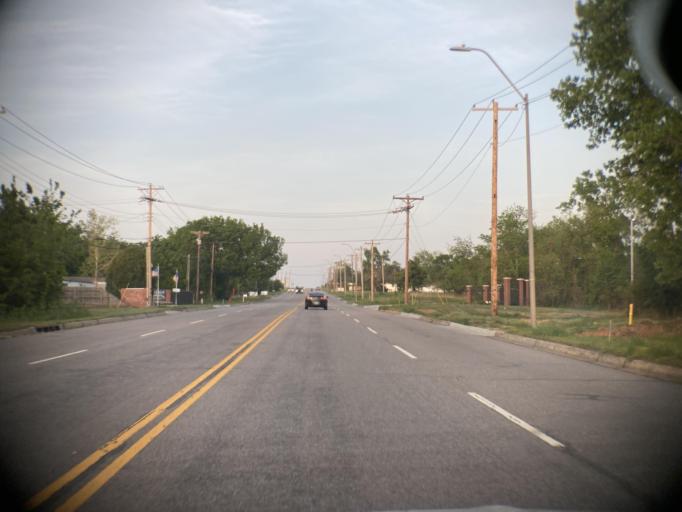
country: US
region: Oklahoma
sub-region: Oklahoma County
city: Midwest City
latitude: 35.4352
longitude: -97.3637
